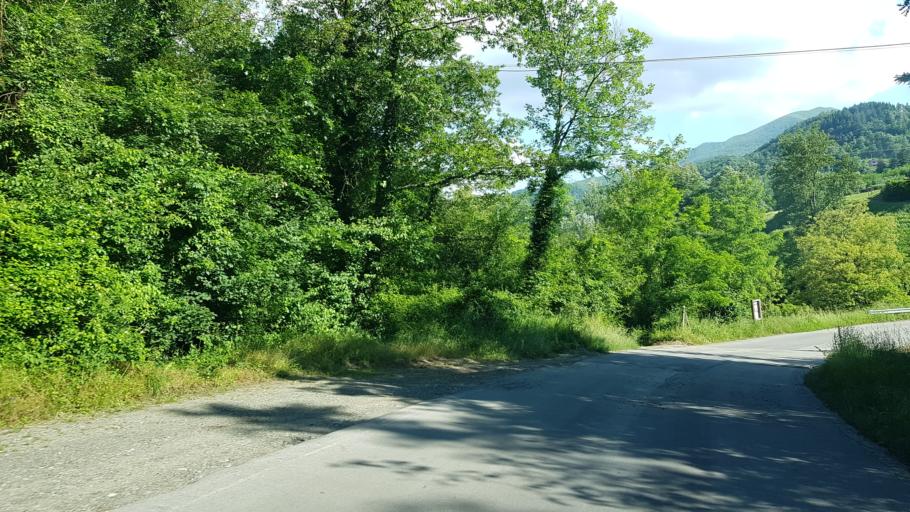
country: IT
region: Tuscany
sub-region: Provincia di Lucca
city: Camporgiano
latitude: 44.1637
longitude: 10.3389
